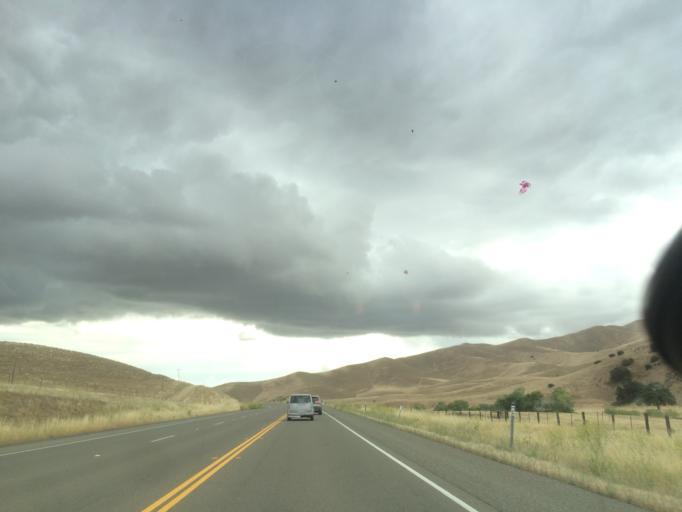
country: US
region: California
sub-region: Kings County
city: Avenal
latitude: 35.7748
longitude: -120.1473
